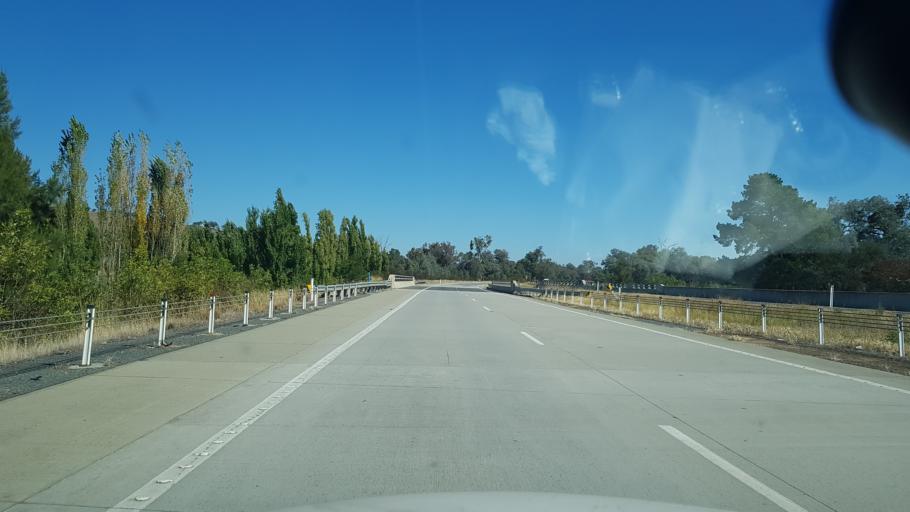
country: AU
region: New South Wales
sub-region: Greater Hume Shire
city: Holbrook
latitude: -35.9003
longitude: 147.1656
